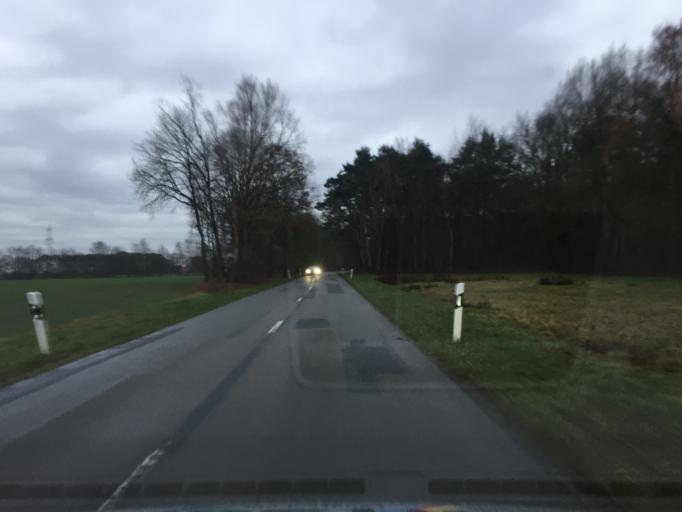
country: DE
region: Lower Saxony
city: Pennigsehl
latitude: 52.6460
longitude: 9.0003
